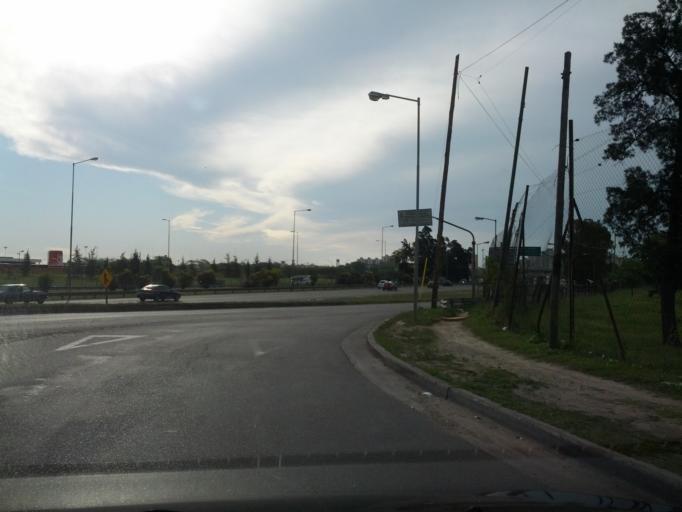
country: AR
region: Buenos Aires F.D.
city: Villa Lugano
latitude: -34.7028
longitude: -58.4628
